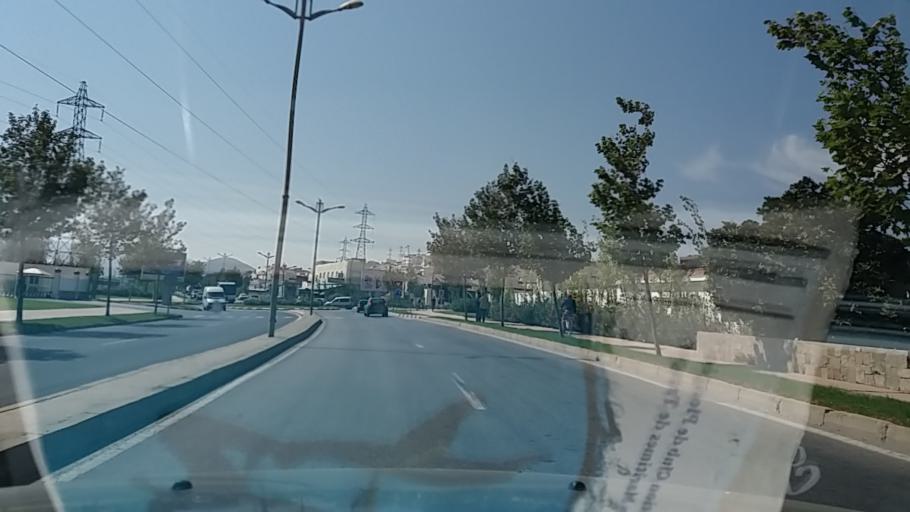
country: MA
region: Tanger-Tetouan
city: Tetouan
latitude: 35.5651
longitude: -5.4206
